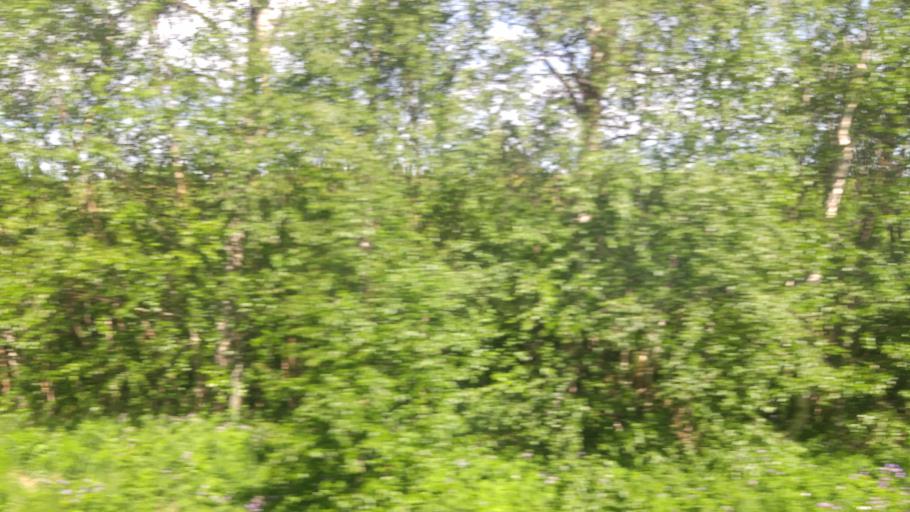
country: SE
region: Jaemtland
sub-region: Are Kommun
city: Are
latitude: 63.3614
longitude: 12.6205
